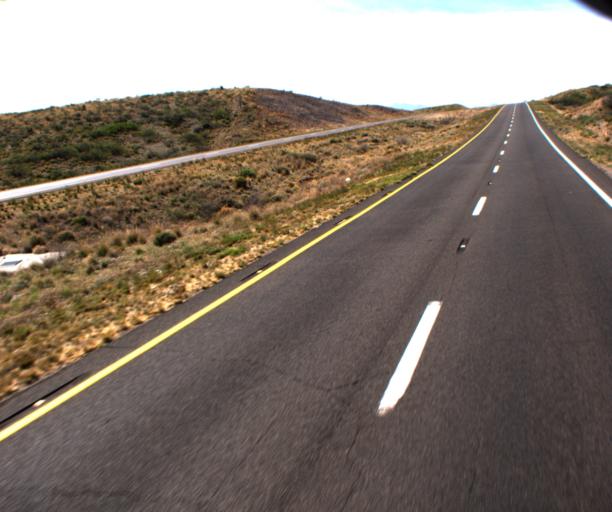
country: US
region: Arizona
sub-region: Graham County
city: Swift Trail Junction
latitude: 32.5114
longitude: -109.6742
